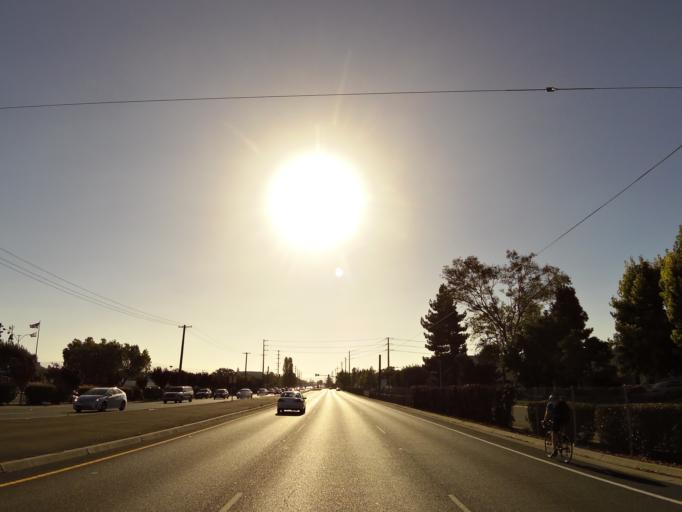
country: US
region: California
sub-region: Santa Clara County
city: Santa Clara
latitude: 37.3745
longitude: -121.9521
